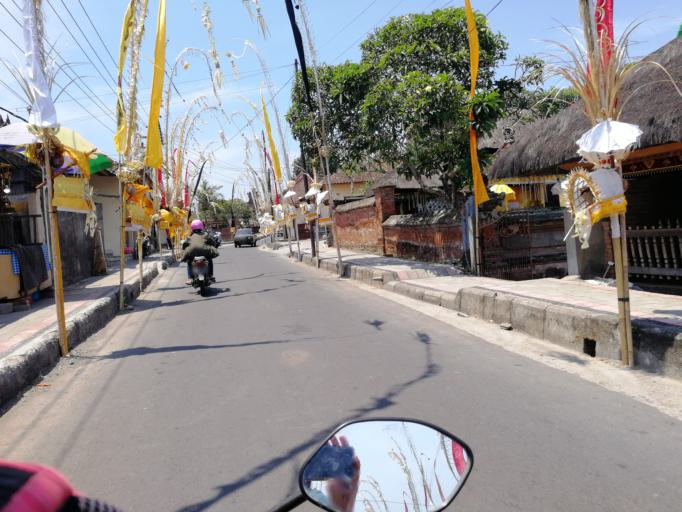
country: ID
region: Bali
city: Banjar Timbrah
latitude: -8.4716
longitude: 115.5914
